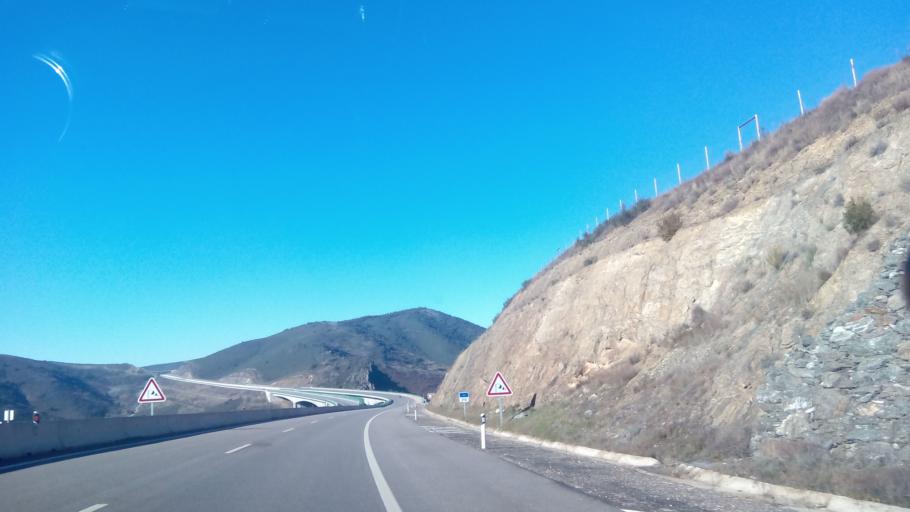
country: PT
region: Braganca
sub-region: Braganca Municipality
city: Braganca
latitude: 41.7725
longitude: -6.6724
